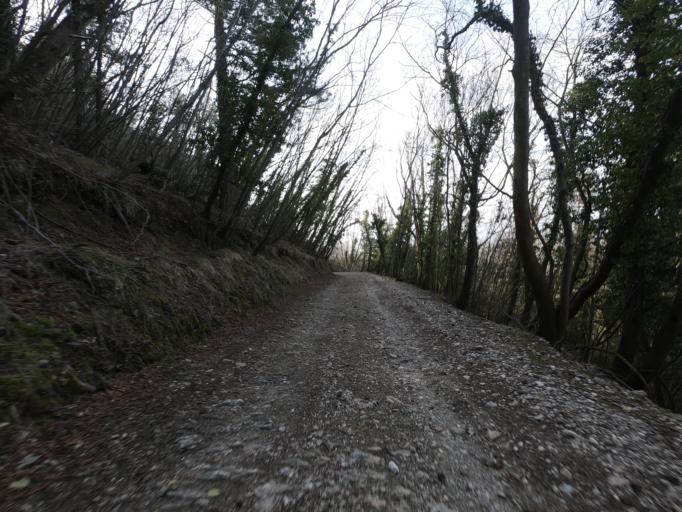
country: IT
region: Liguria
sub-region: Provincia di Savona
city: Zuccarello
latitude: 44.1193
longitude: 8.1430
